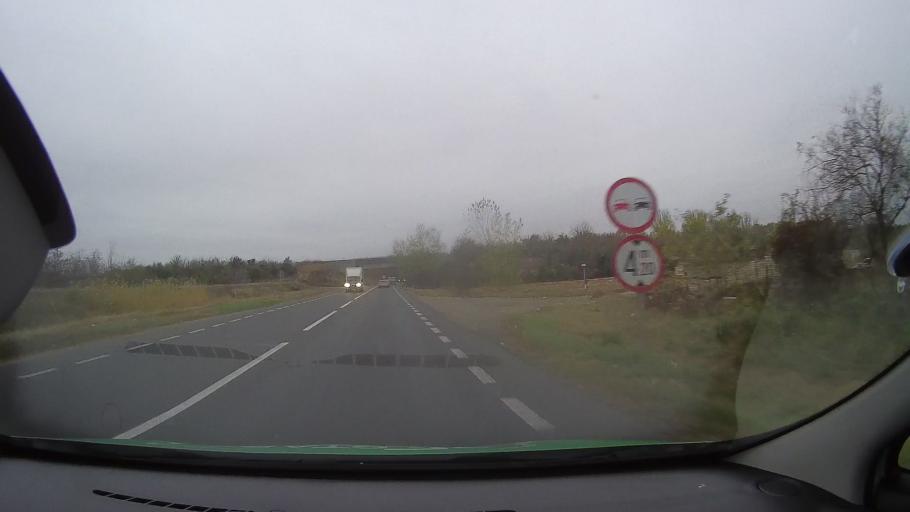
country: RO
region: Ialomita
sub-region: Comuna Slobozia
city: Slobozia
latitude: 44.5538
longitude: 27.3580
